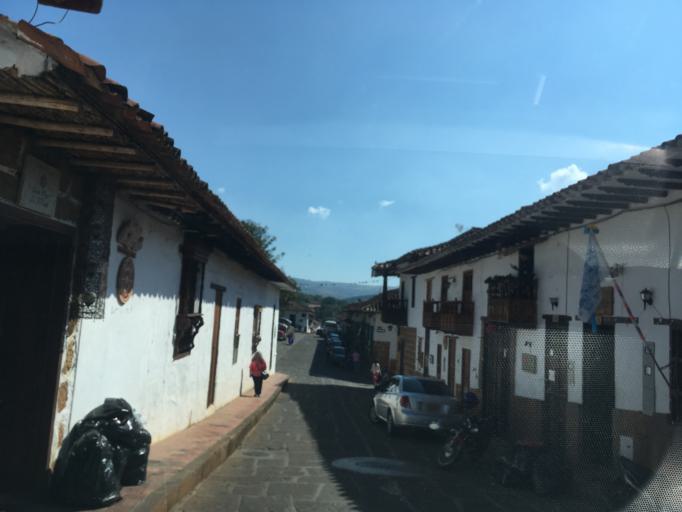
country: CO
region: Santander
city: Barichara
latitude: 6.6354
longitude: -73.2241
